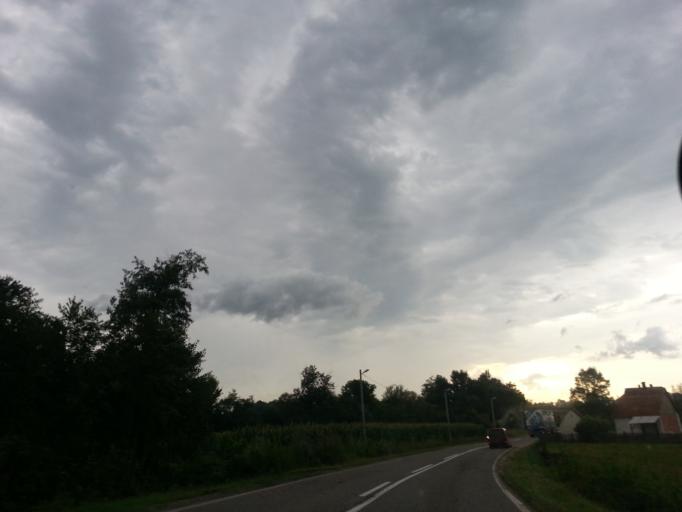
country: BA
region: Republika Srpska
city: Velika Obarska
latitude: 44.7834
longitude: 19.0950
